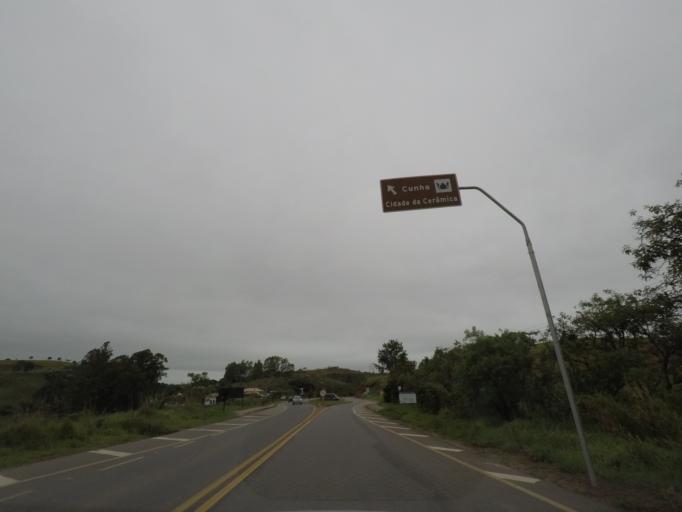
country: BR
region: Sao Paulo
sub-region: Cunha
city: Cunha
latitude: -23.0606
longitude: -44.9711
